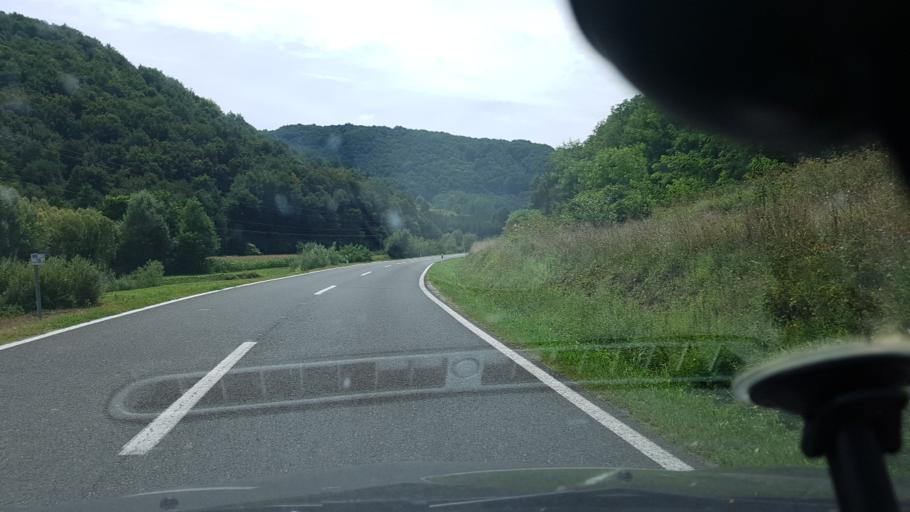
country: HR
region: Varazdinska
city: Lepoglava
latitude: 46.2144
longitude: 16.0038
